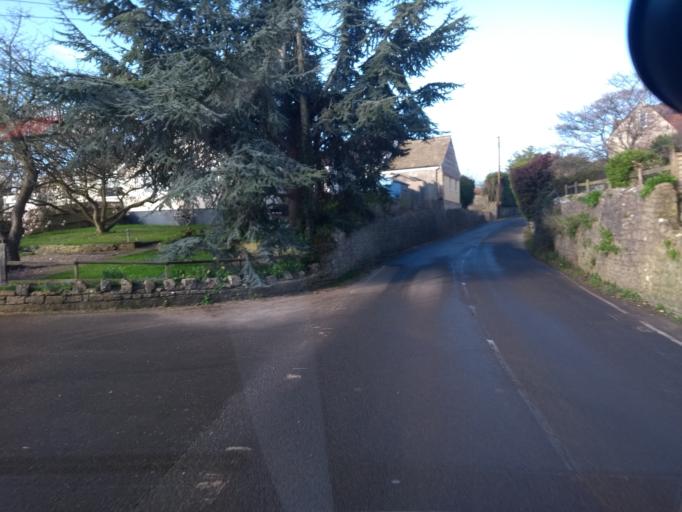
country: GB
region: England
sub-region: Somerset
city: Woolavington
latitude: 51.1559
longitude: -2.8962
